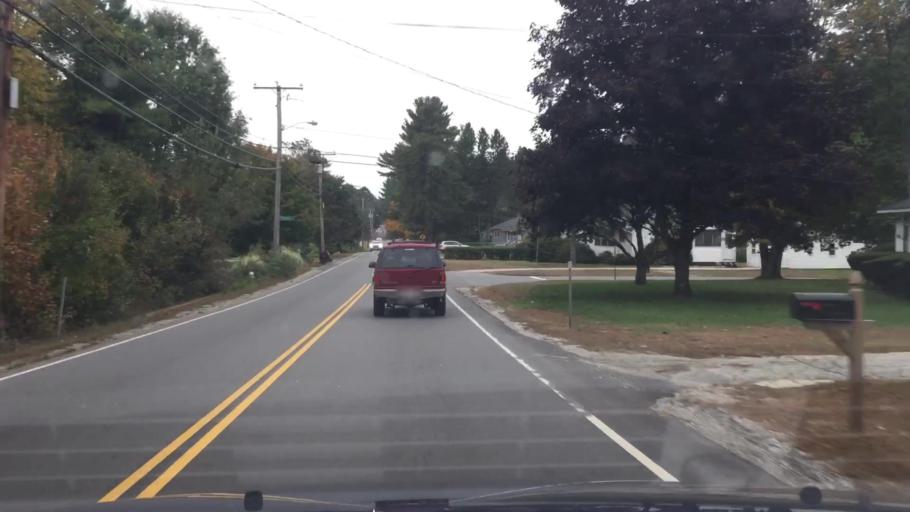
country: US
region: Massachusetts
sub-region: Middlesex County
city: Tyngsboro
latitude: 42.7145
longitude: -71.4120
